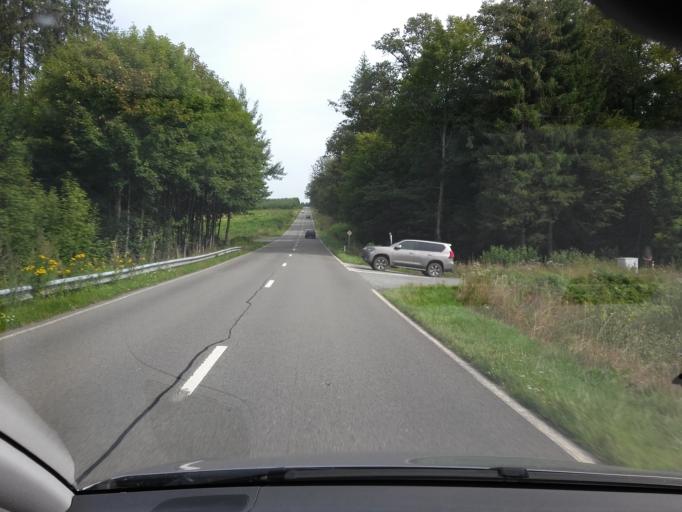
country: BE
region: Wallonia
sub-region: Province du Luxembourg
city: Chiny
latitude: 49.7611
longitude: 5.3187
